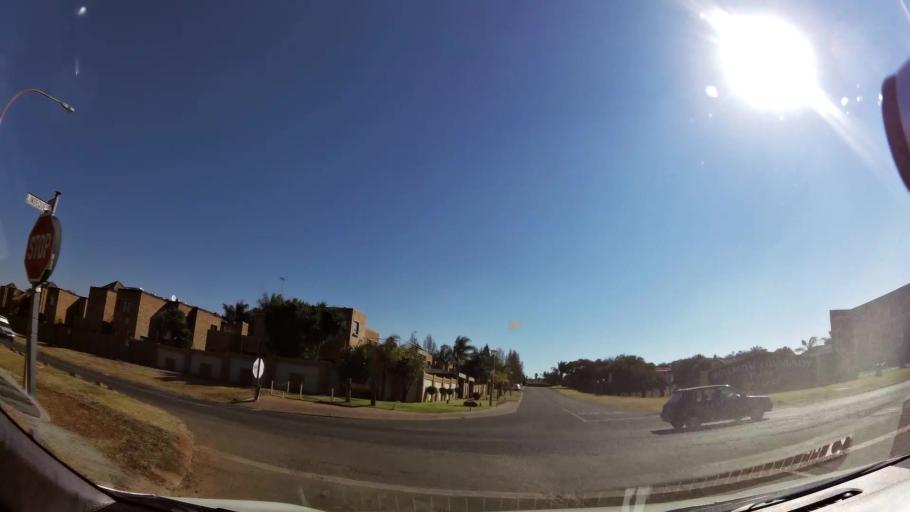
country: ZA
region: Gauteng
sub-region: Ekurhuleni Metropolitan Municipality
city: Germiston
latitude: -26.2992
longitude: 28.0965
